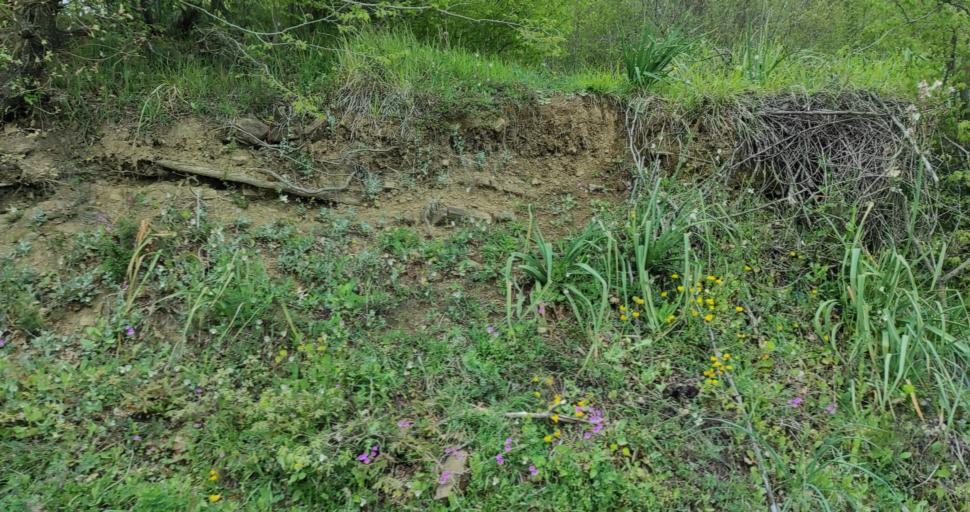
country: AL
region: Shkoder
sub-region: Rrethi i Shkodres
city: Dajc
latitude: 42.0219
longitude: 19.4256
